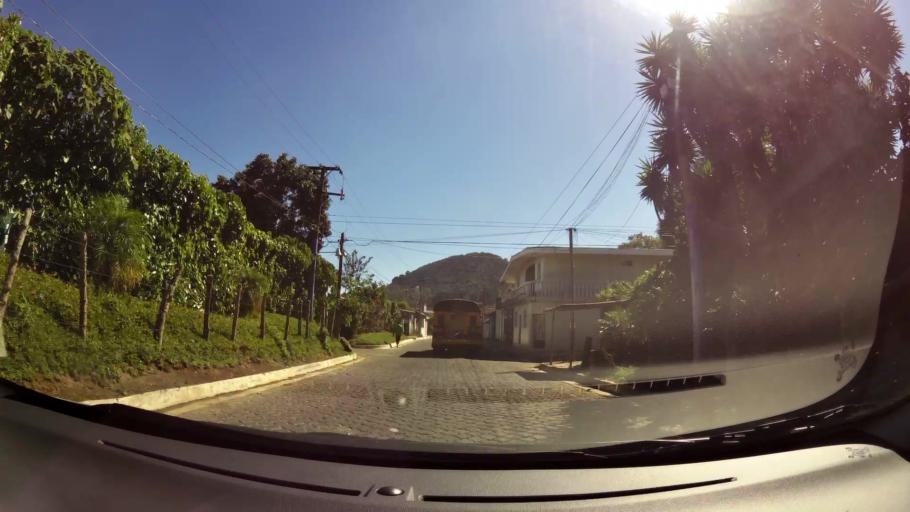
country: SV
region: Ahuachapan
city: Concepcion de Ataco
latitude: 13.8581
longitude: -89.8065
